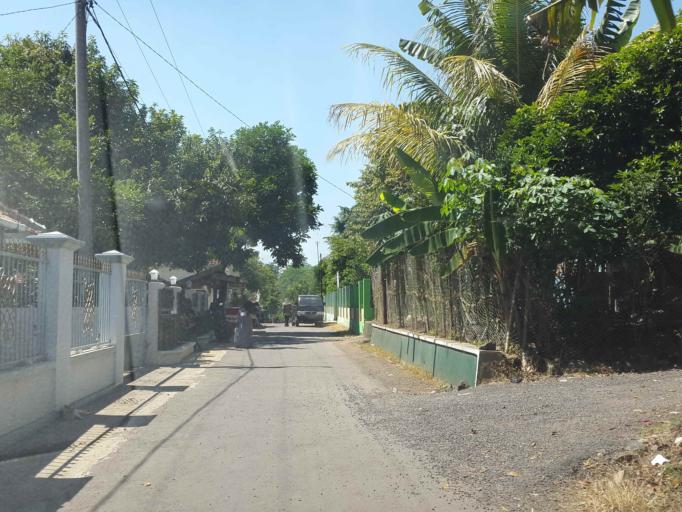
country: ID
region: West Java
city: Ciranjang-hilir
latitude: -6.7910
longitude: 107.2587
